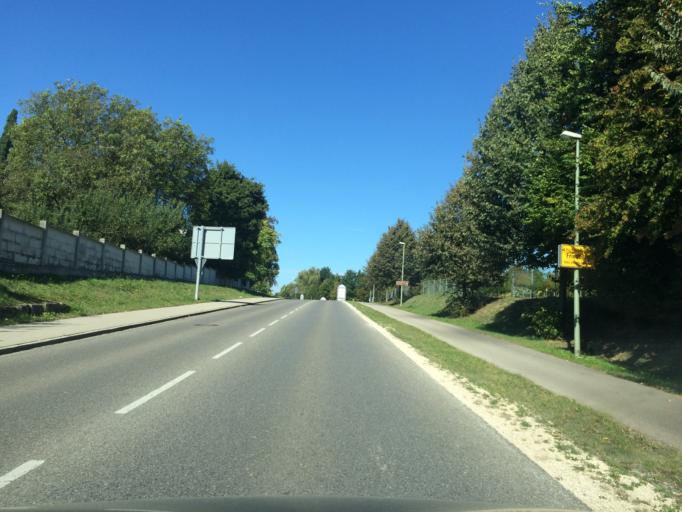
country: DE
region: Bavaria
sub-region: Swabia
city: Friedberg
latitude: 48.3472
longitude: 10.9937
